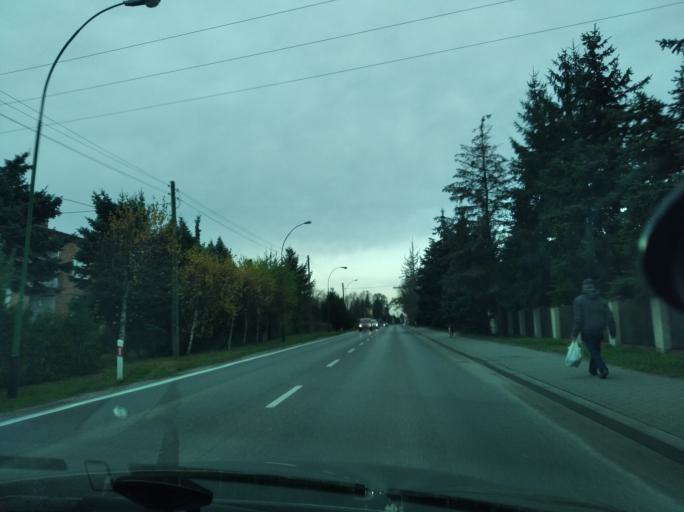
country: PL
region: Subcarpathian Voivodeship
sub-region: Powiat lancucki
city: Lancut
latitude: 50.0928
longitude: 22.2314
